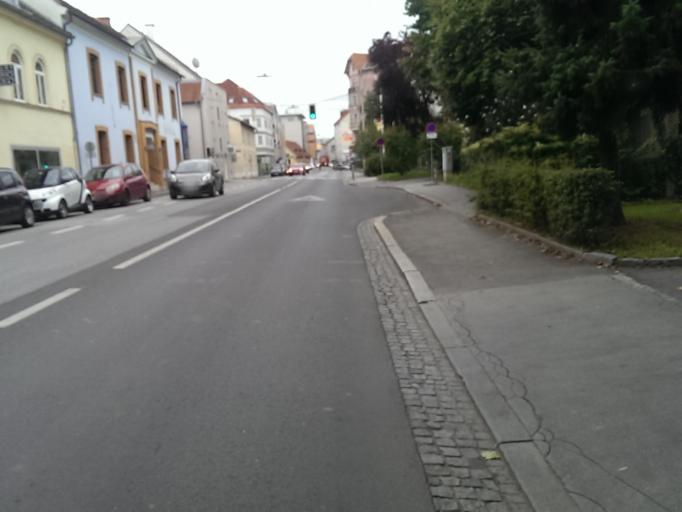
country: AT
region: Styria
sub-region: Graz Stadt
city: Graz
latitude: 47.0673
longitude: 15.4620
